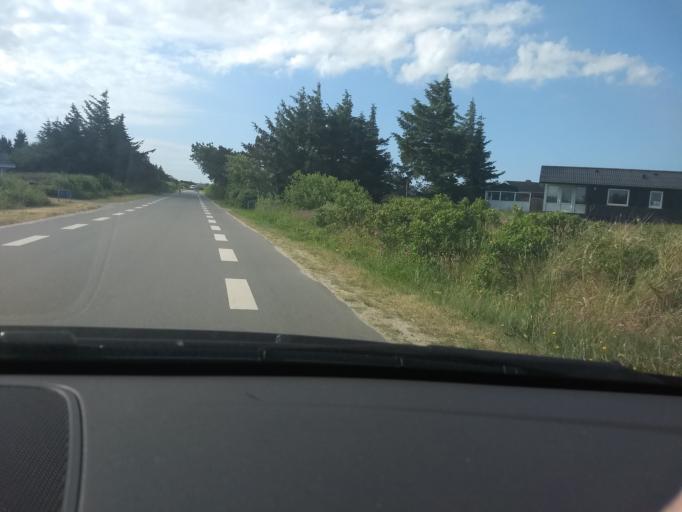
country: DE
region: Schleswig-Holstein
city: List
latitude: 55.1432
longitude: 8.4942
